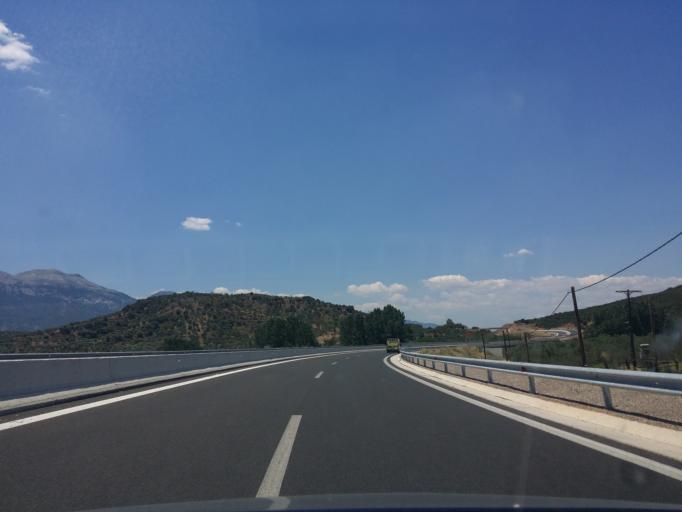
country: GR
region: Peloponnese
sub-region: Nomos Lakonias
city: Magoula
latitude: 37.1198
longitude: 22.4136
